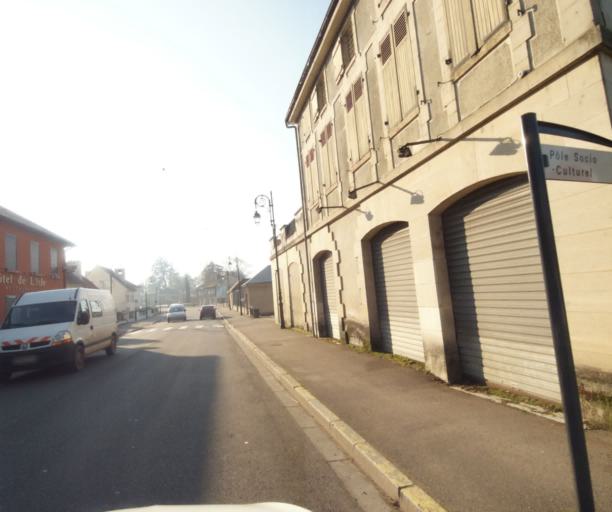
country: FR
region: Champagne-Ardenne
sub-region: Departement de la Haute-Marne
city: Montier-en-Der
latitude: 48.4794
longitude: 4.7687
